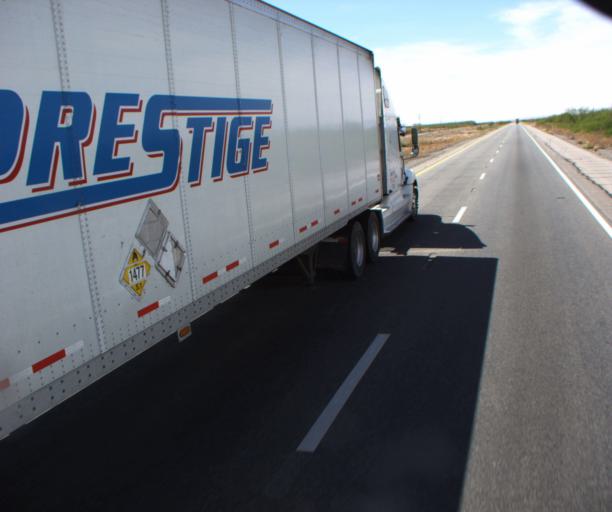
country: US
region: Arizona
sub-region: Cochise County
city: Willcox
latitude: 32.2912
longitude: -109.3260
